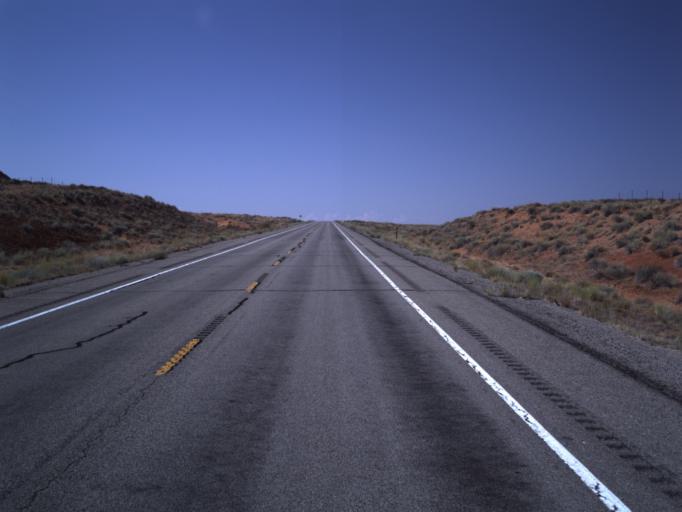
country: US
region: Utah
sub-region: San Juan County
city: Blanding
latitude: 37.2367
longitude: -109.6103
